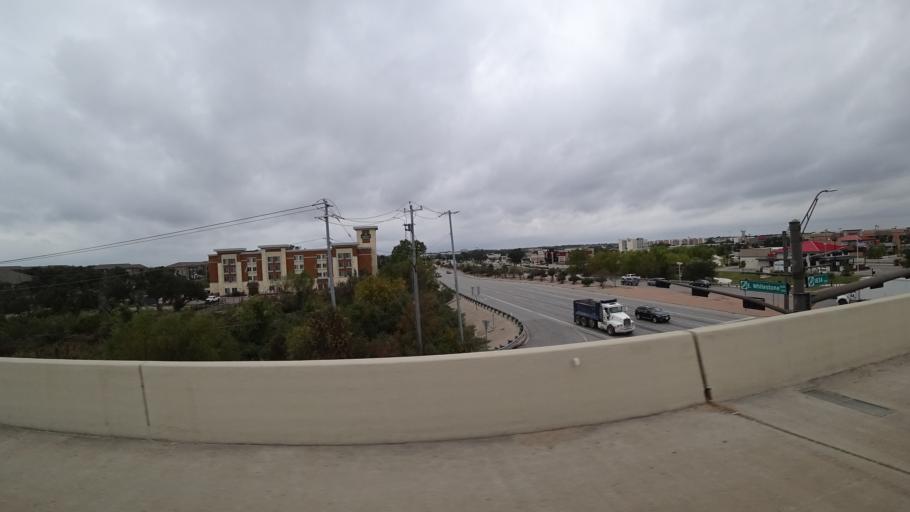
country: US
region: Texas
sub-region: Williamson County
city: Cedar Park
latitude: 30.5251
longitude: -97.8165
